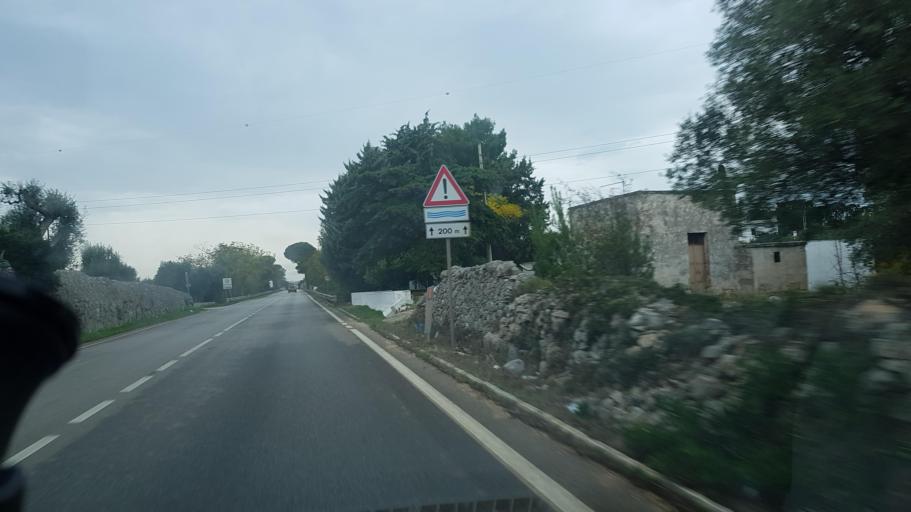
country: IT
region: Apulia
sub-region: Provincia di Brindisi
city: Carovigno
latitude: 40.7162
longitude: 17.6195
